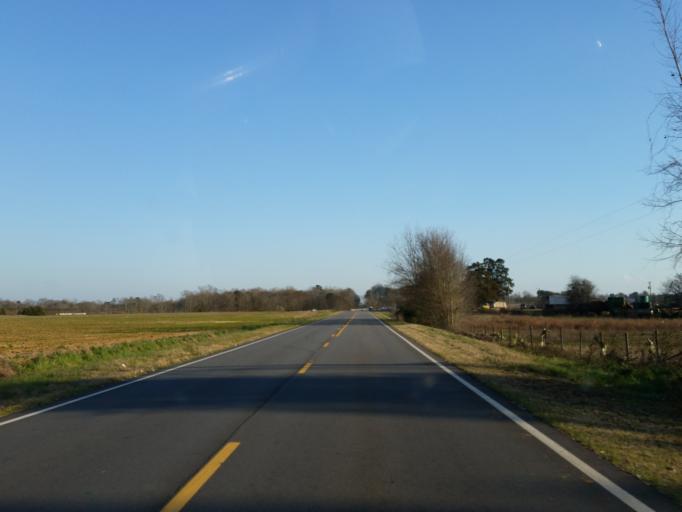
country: US
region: Georgia
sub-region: Dooly County
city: Unadilla
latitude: 32.3065
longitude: -83.7654
